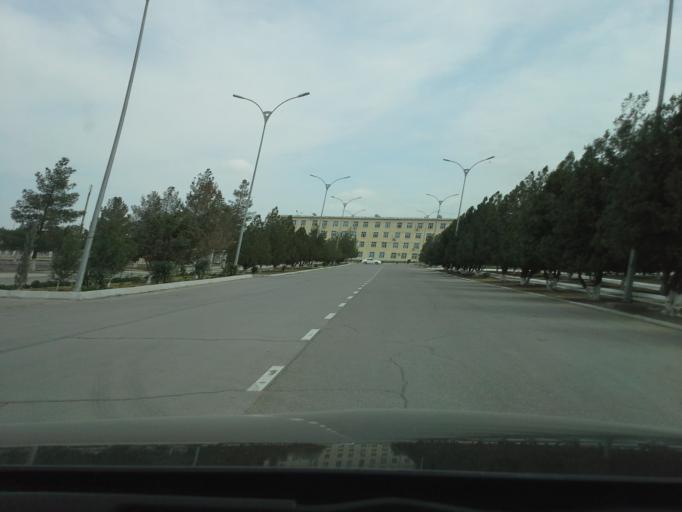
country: TM
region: Ahal
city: Abadan
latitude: 38.0563
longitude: 58.1477
